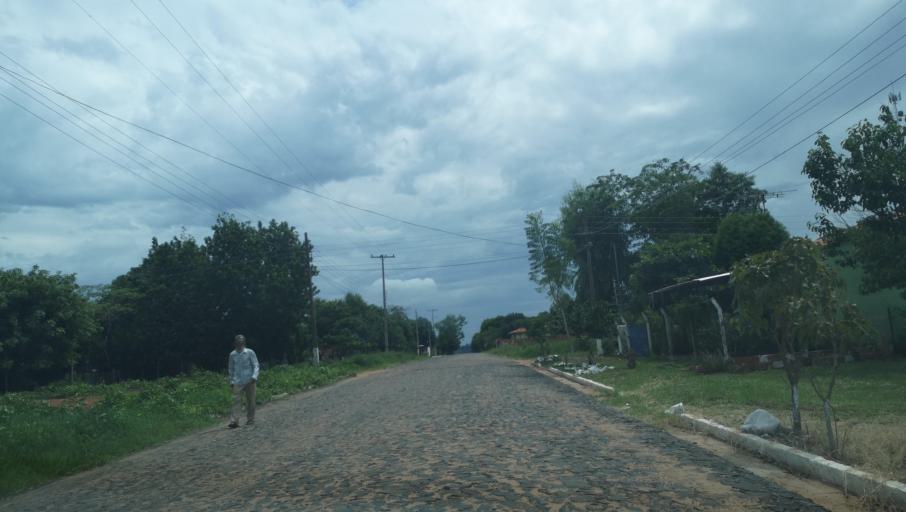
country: PY
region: San Pedro
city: Capiibary
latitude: -24.7257
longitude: -56.0112
